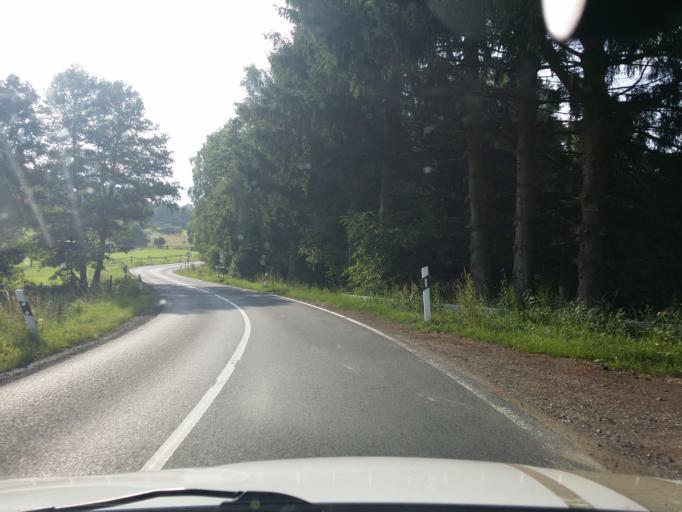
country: DE
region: Hesse
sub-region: Regierungsbezirk Darmstadt
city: Glashutten
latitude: 50.1922
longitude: 8.3917
